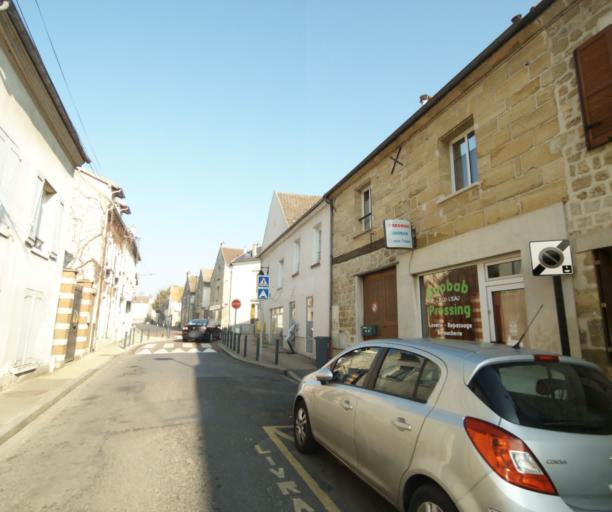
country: FR
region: Ile-de-France
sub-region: Departement du Val-d'Oise
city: Cergy
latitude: 49.0414
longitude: 2.0586
